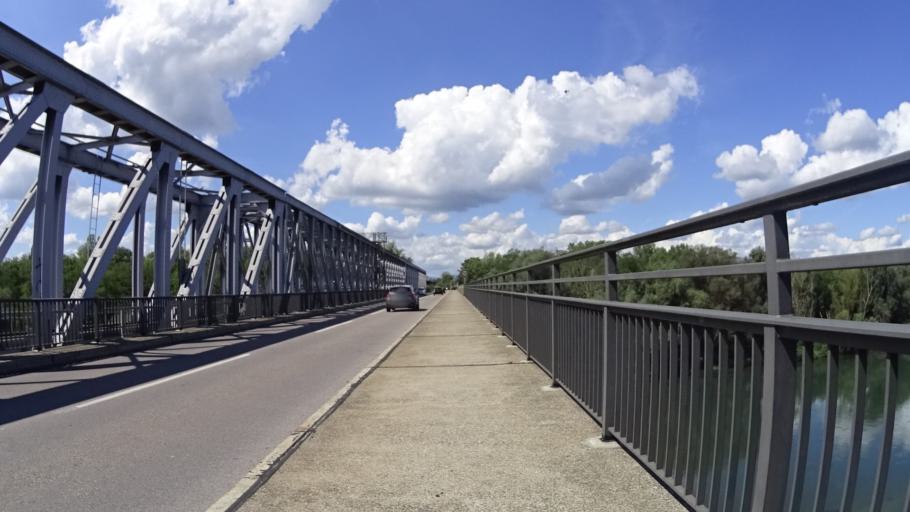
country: FR
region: Alsace
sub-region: Departement du Haut-Rhin
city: Chalampe
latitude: 47.8145
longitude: 7.5473
